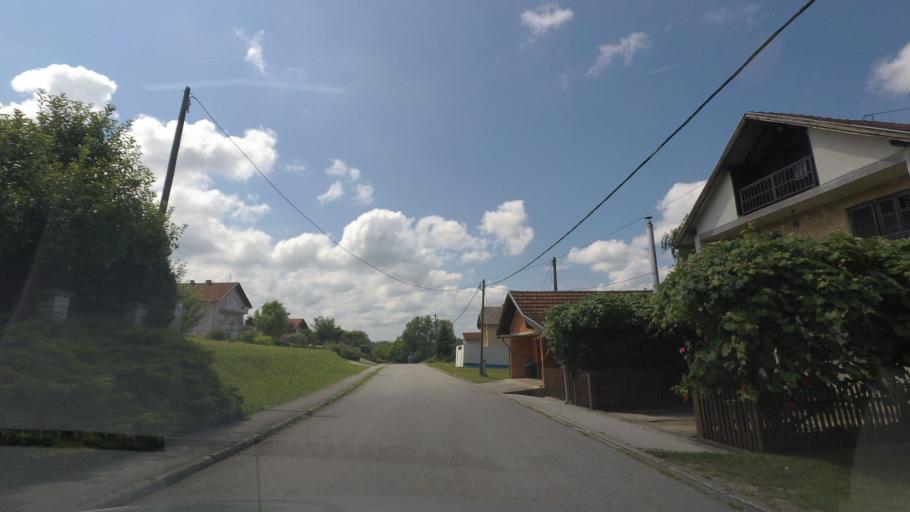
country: HR
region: Sisacko-Moslavacka
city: Gvozd
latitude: 45.3060
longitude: 15.9700
